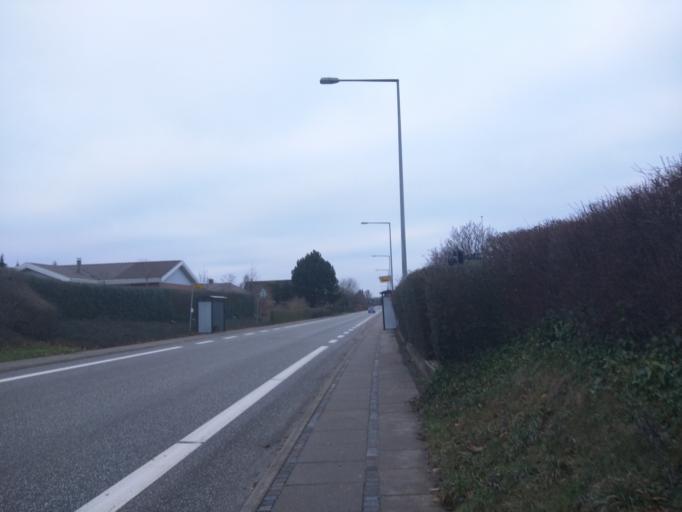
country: DK
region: South Denmark
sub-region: Fredericia Kommune
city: Snoghoj
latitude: 55.5308
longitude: 9.7302
